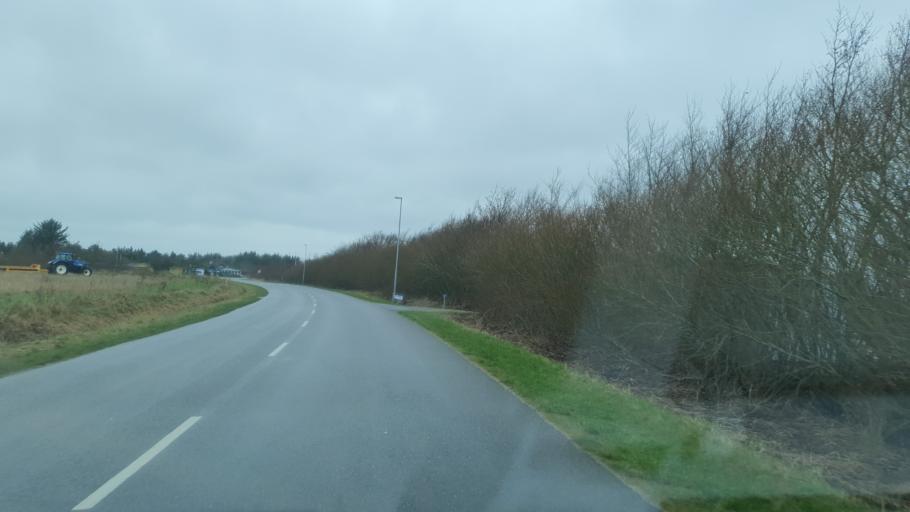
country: DK
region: North Denmark
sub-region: Jammerbugt Kommune
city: Fjerritslev
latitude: 57.1350
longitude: 9.1292
